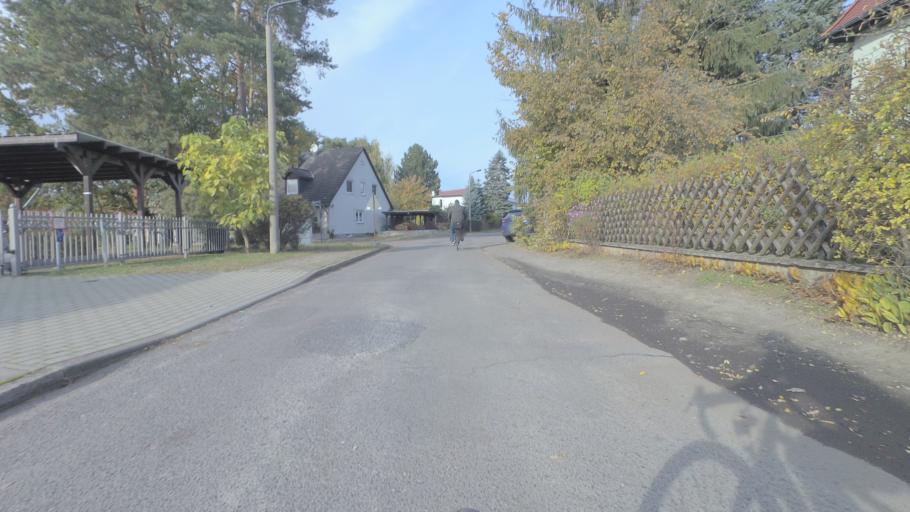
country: DE
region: Brandenburg
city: Ludwigsfelde
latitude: 52.2931
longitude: 13.2469
